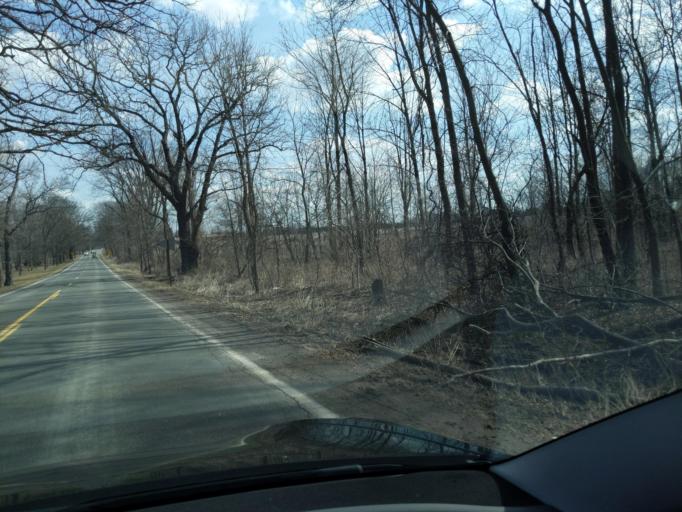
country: US
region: Michigan
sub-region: Washtenaw County
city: Dexter
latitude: 42.3841
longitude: -83.8880
